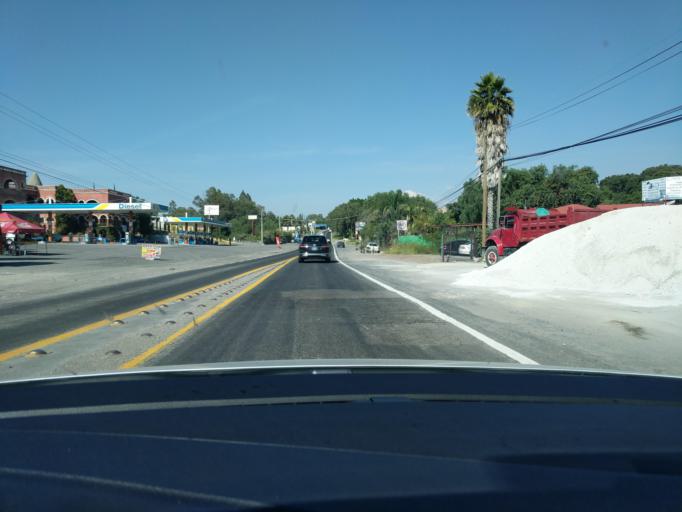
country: MX
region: Puebla
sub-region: Atlixco
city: San Agustin Huixaxtla
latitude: 18.9282
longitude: -98.4090
